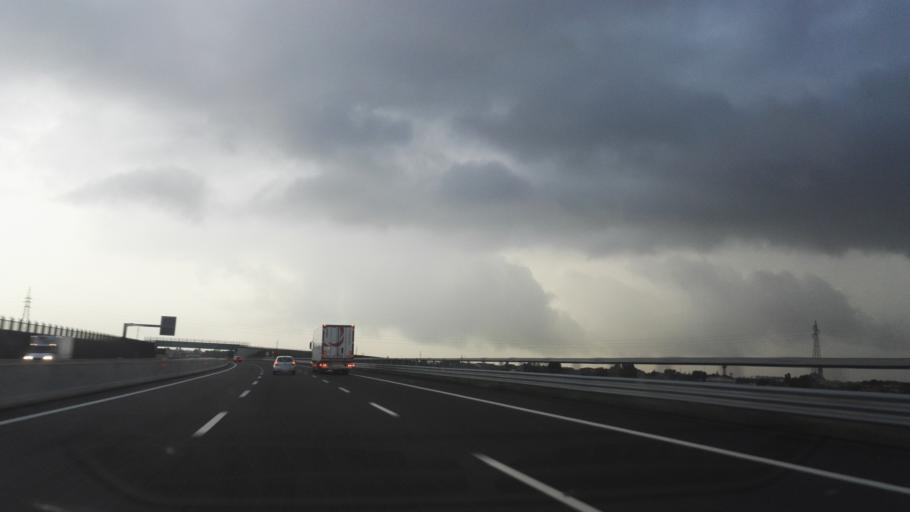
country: IT
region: Lombardy
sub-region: Citta metropolitana di Milano
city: Bellinzago Lombardo
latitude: 45.5297
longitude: 9.4396
